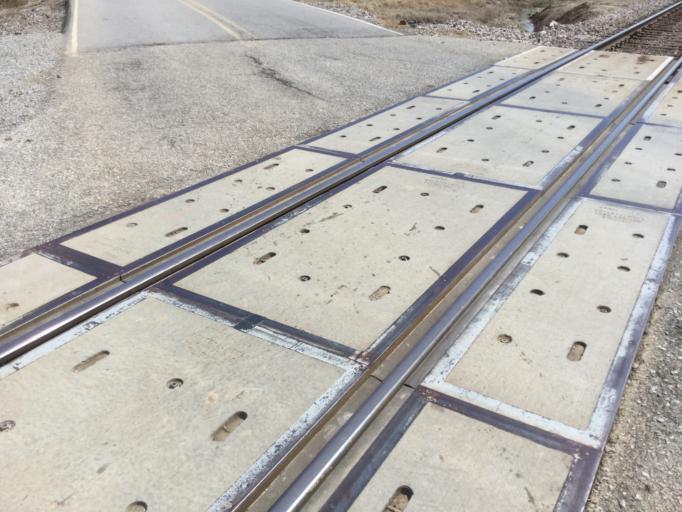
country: US
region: Kansas
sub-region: Cherokee County
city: Columbus
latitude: 37.1341
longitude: -94.8257
